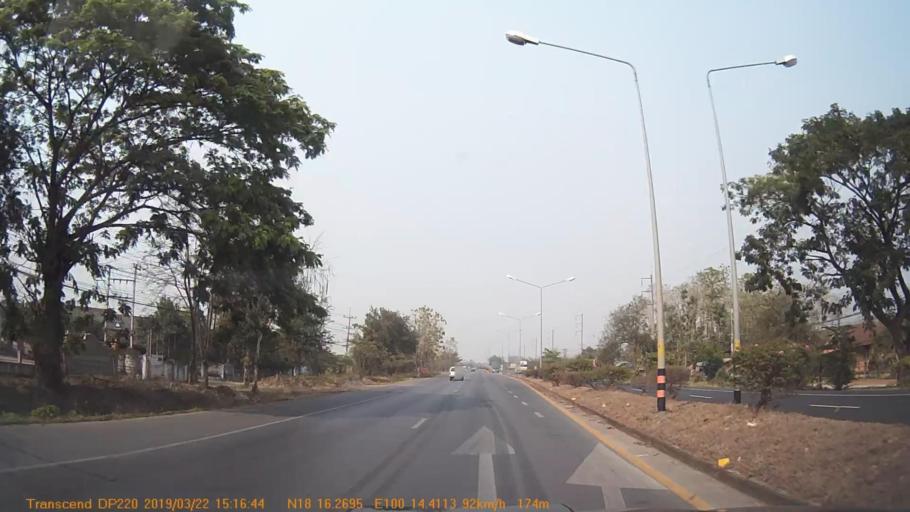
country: TH
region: Phrae
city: Nong Muang Khai
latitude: 18.2716
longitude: 100.2405
